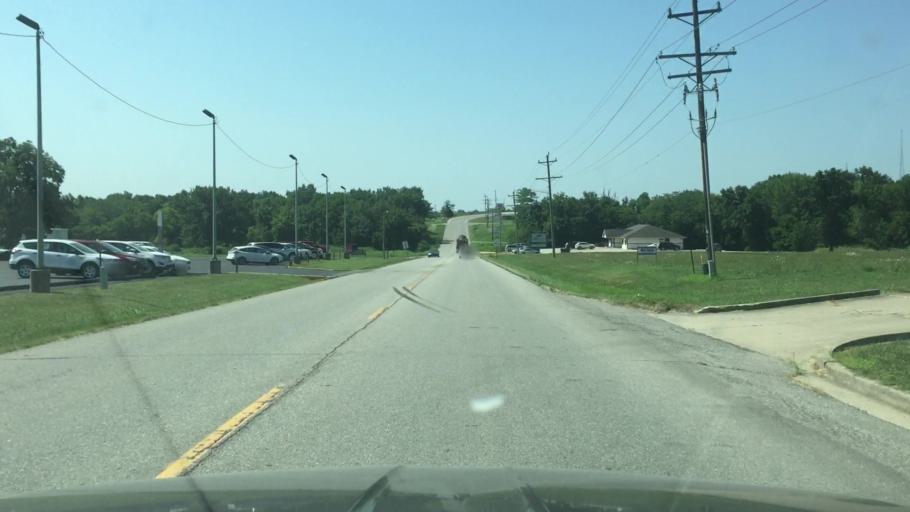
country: US
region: Missouri
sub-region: Moniteau County
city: Tipton
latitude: 38.6480
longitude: -92.7841
